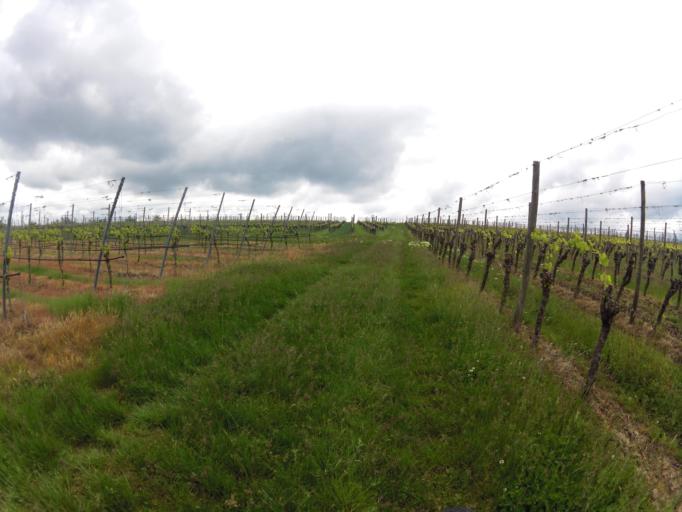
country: DE
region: Bavaria
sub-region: Regierungsbezirk Unterfranken
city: Volkach
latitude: 49.8757
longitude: 10.2207
